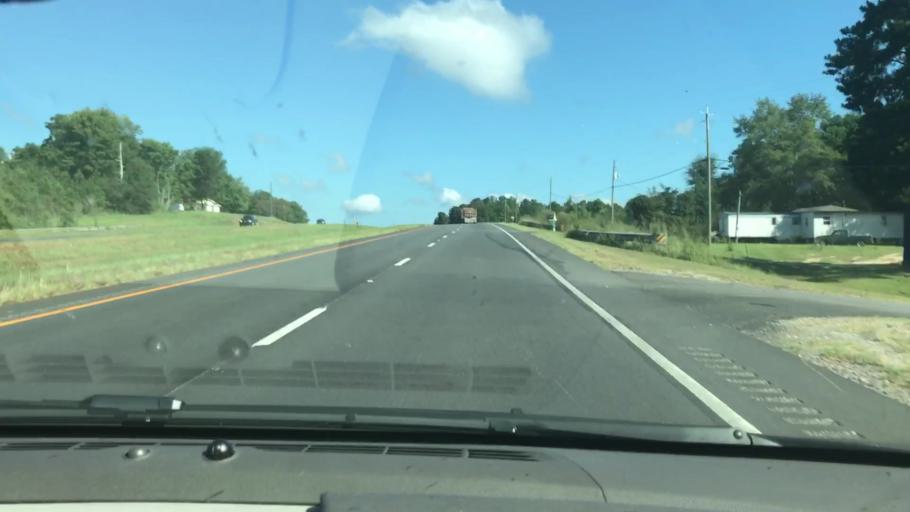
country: US
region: Alabama
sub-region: Barbour County
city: Eufaula
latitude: 32.0265
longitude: -85.1199
